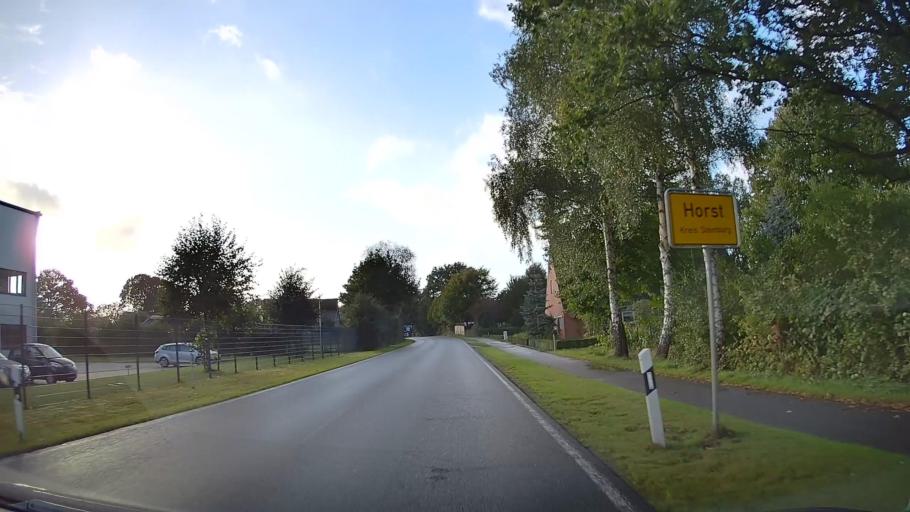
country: DE
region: Schleswig-Holstein
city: Horst
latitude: 53.8021
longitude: 9.6570
